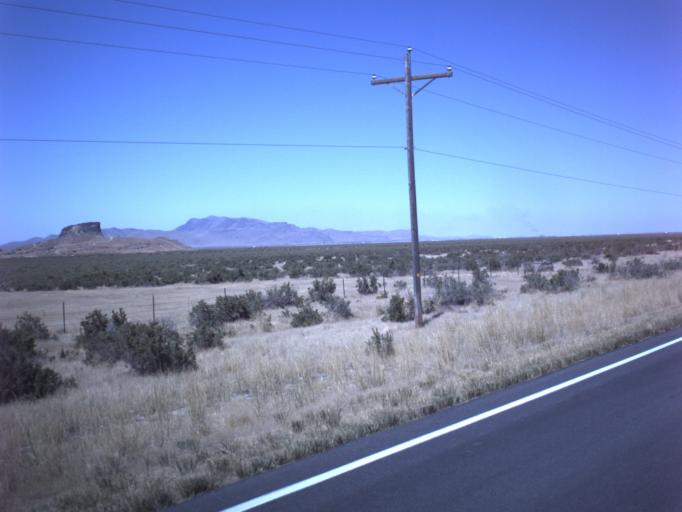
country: US
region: Utah
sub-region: Tooele County
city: Grantsville
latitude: 40.6941
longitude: -112.6675
